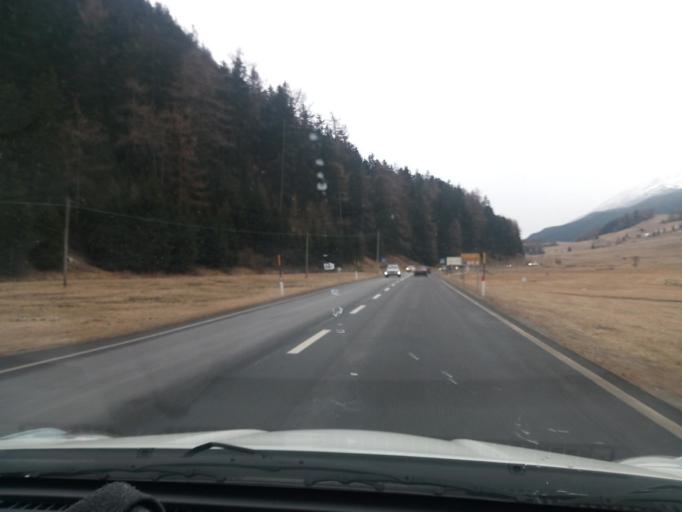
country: AT
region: Tyrol
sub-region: Politischer Bezirk Landeck
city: Nauders
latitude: 46.8449
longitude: 10.5064
